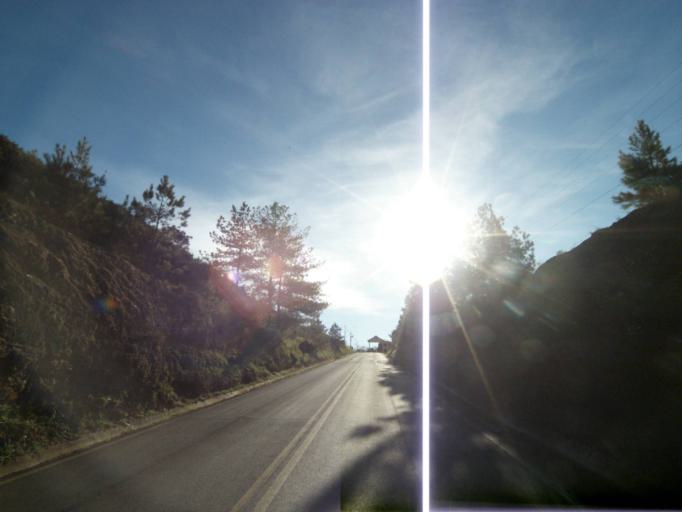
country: BR
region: Parana
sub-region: Tibagi
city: Tibagi
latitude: -24.5277
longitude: -50.3992
